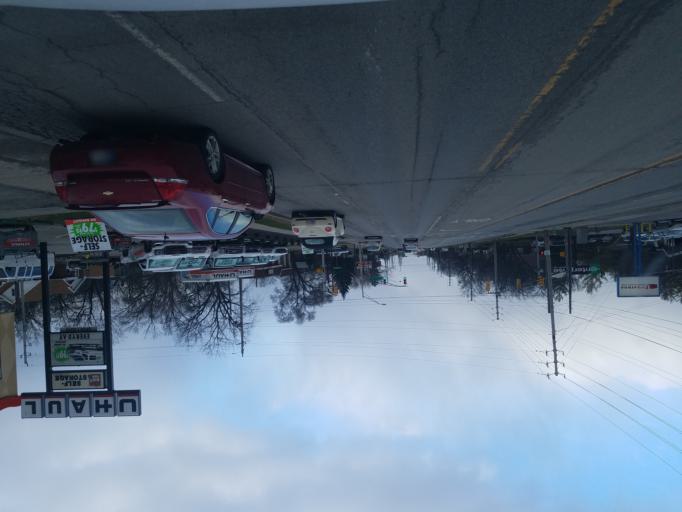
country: US
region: Indiana
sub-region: Marion County
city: Warren Park
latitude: 39.7715
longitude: -86.0555
